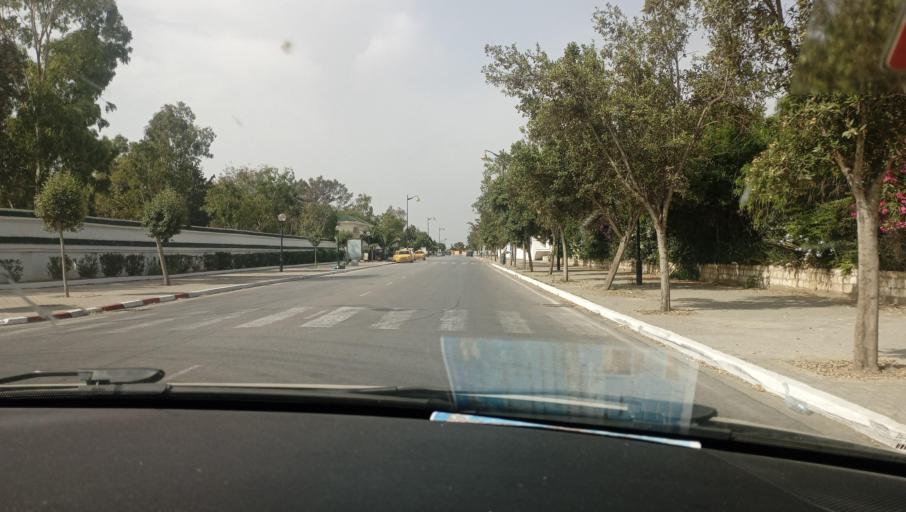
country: TN
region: Nabul
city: Al Hammamat
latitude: 36.3585
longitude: 10.5288
